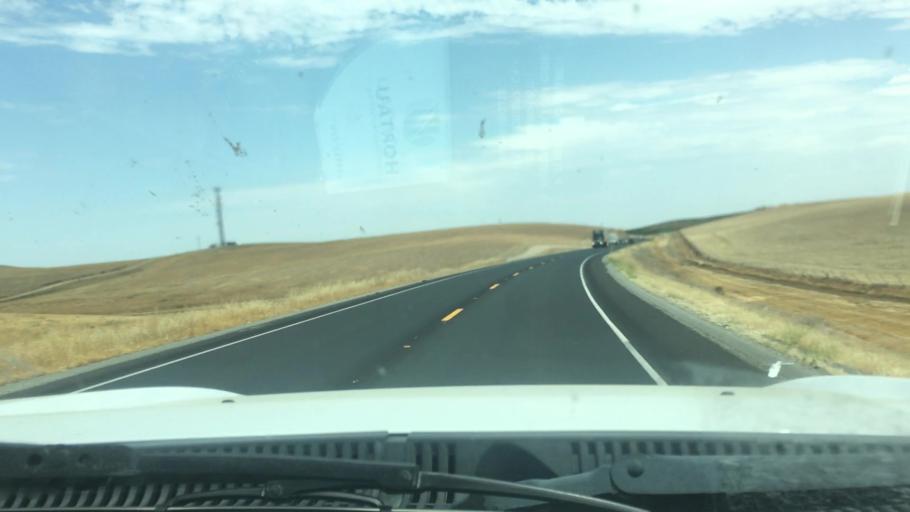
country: US
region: California
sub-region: Tulare County
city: Richgrove
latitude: 35.6524
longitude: -119.0798
